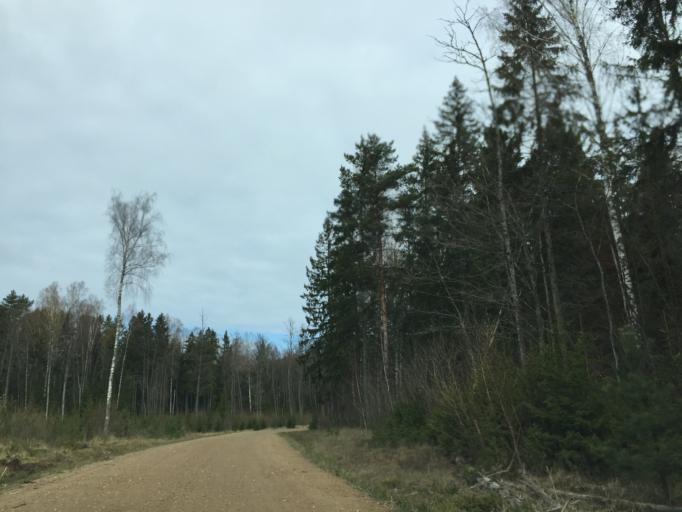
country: LV
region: Saulkrastu
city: Saulkrasti
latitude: 57.5071
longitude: 24.4147
